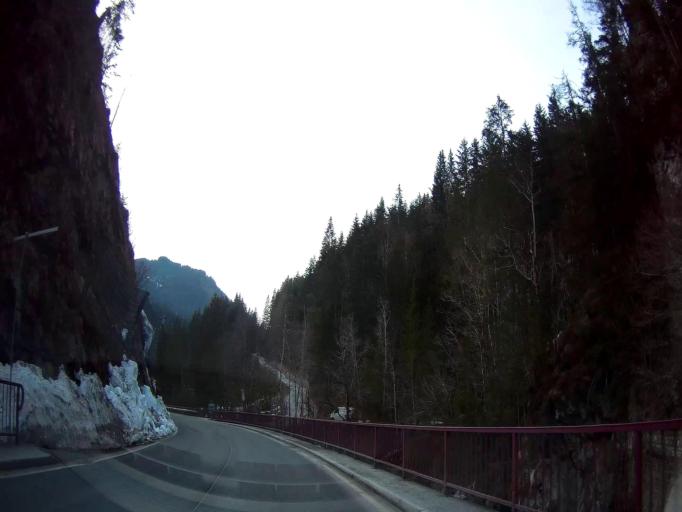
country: AT
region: Salzburg
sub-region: Politischer Bezirk Hallein
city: Abtenau
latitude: 47.5450
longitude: 13.4192
